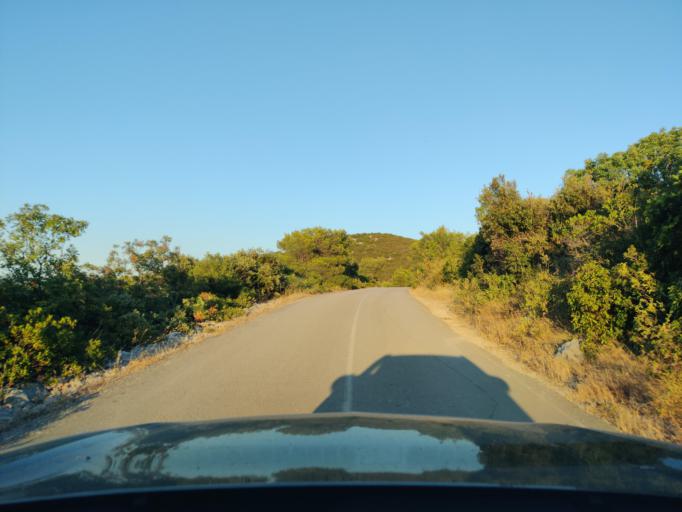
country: HR
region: Sibensko-Kniniska
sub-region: Grad Sibenik
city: Tisno
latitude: 43.8096
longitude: 15.6323
